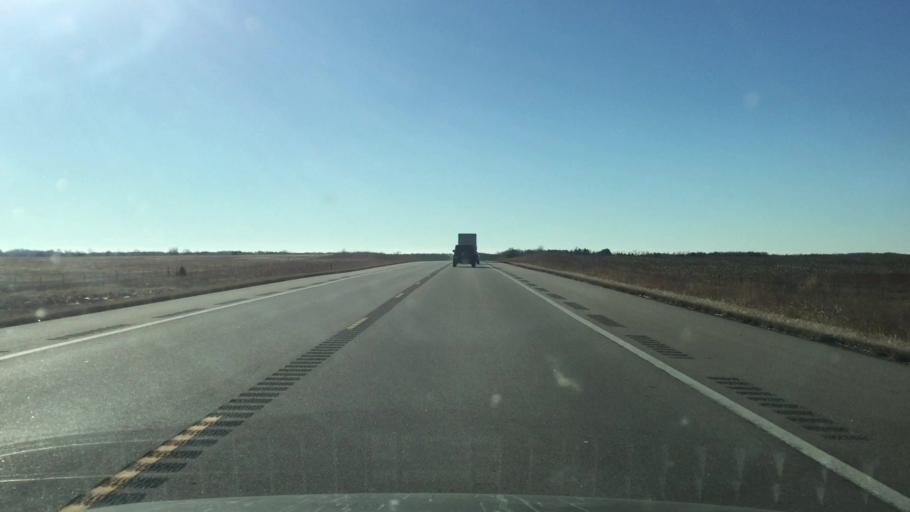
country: US
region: Kansas
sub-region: Allen County
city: Iola
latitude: 38.0503
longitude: -95.3804
